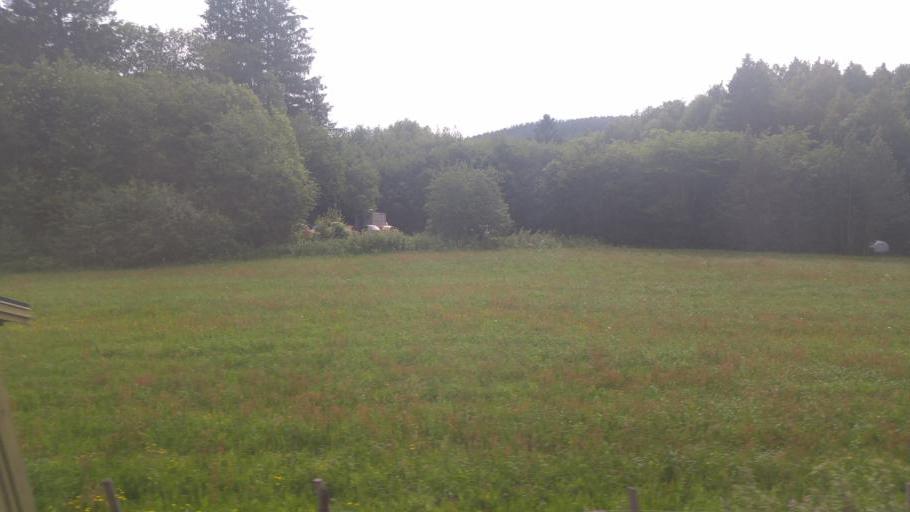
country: NO
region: Sor-Trondelag
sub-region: Melhus
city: Lundamo
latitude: 63.1742
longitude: 10.3060
